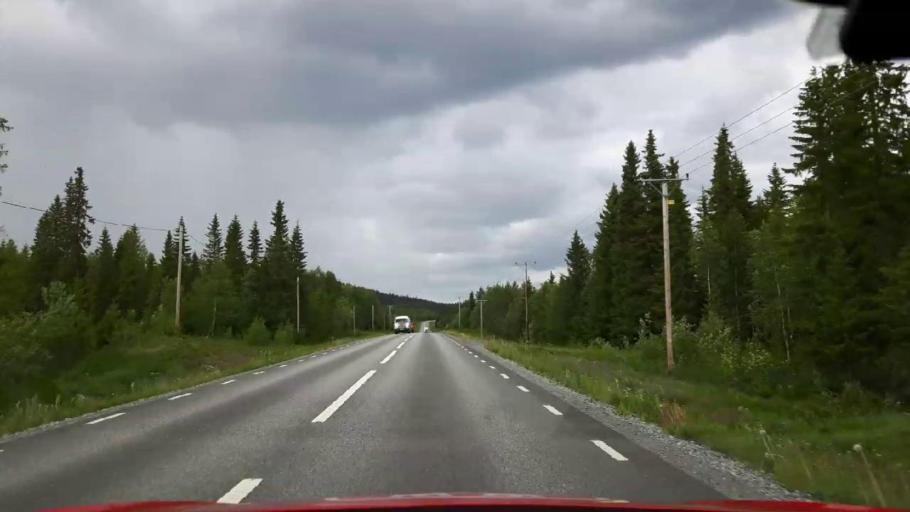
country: SE
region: Jaemtland
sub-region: Krokoms Kommun
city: Krokom
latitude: 63.6858
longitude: 14.3270
